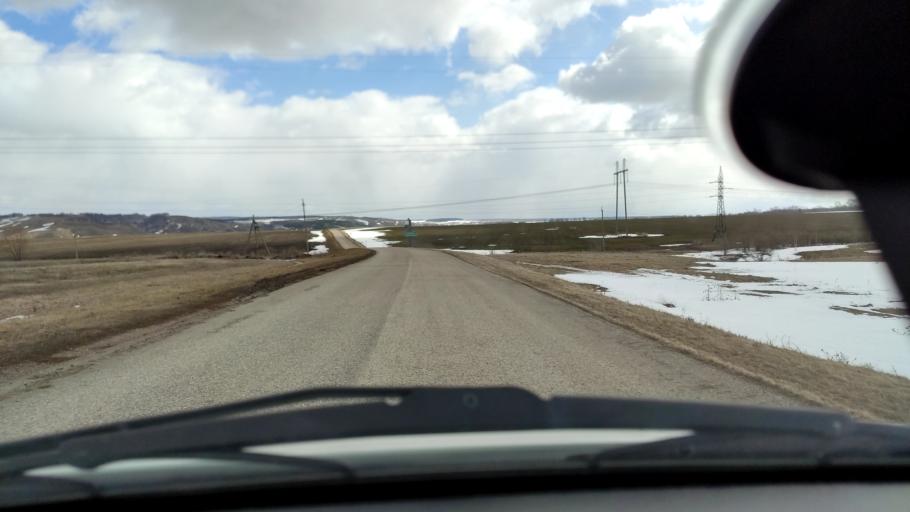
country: RU
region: Bashkortostan
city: Tolbazy
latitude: 54.1704
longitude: 55.9169
